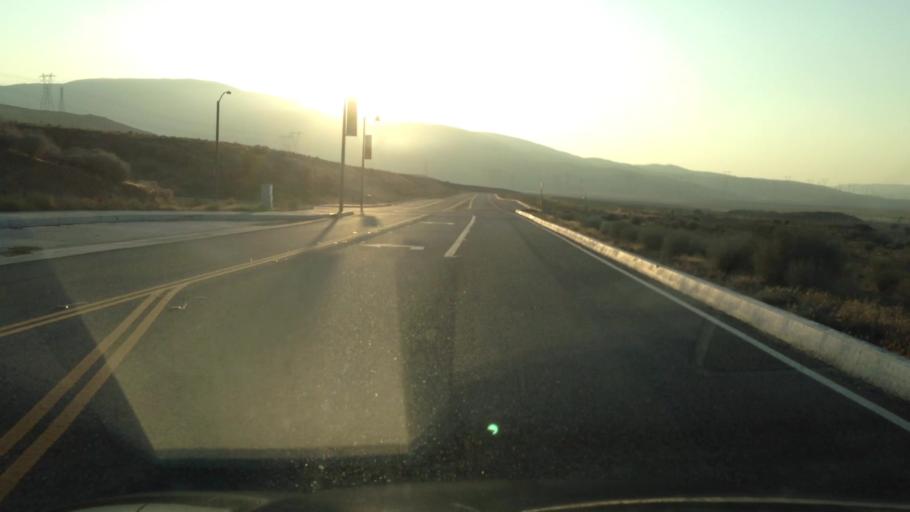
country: US
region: California
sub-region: Los Angeles County
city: Desert View Highlands
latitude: 34.5677
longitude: -118.1801
